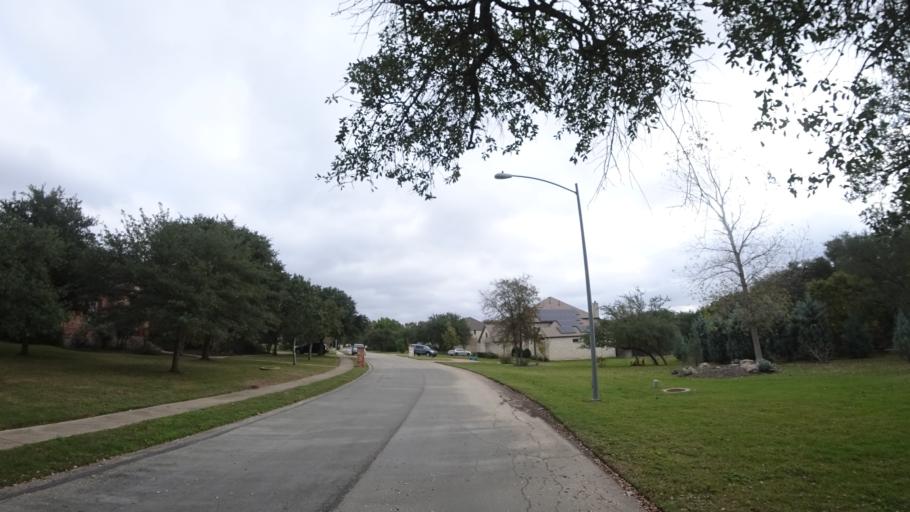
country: US
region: Texas
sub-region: Travis County
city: Barton Creek
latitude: 30.2549
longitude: -97.9095
